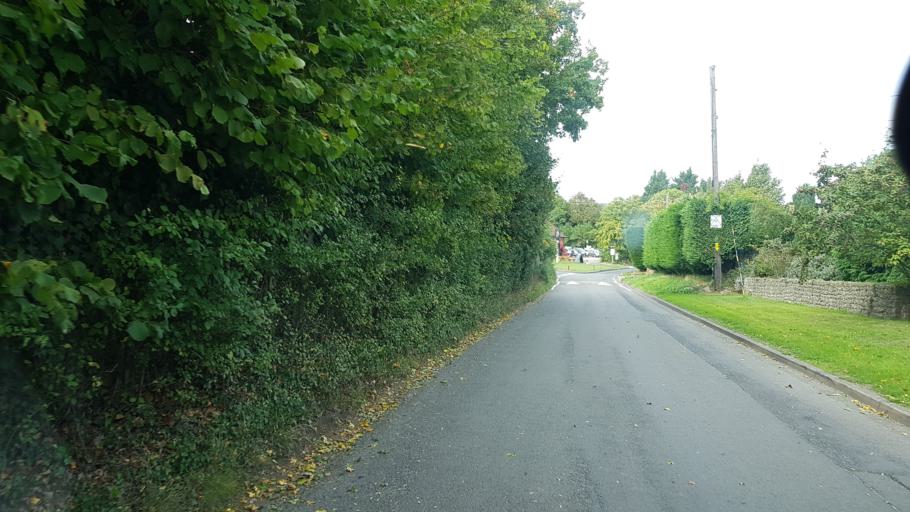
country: GB
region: England
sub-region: Kent
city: Meopham
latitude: 51.3144
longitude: 0.3547
